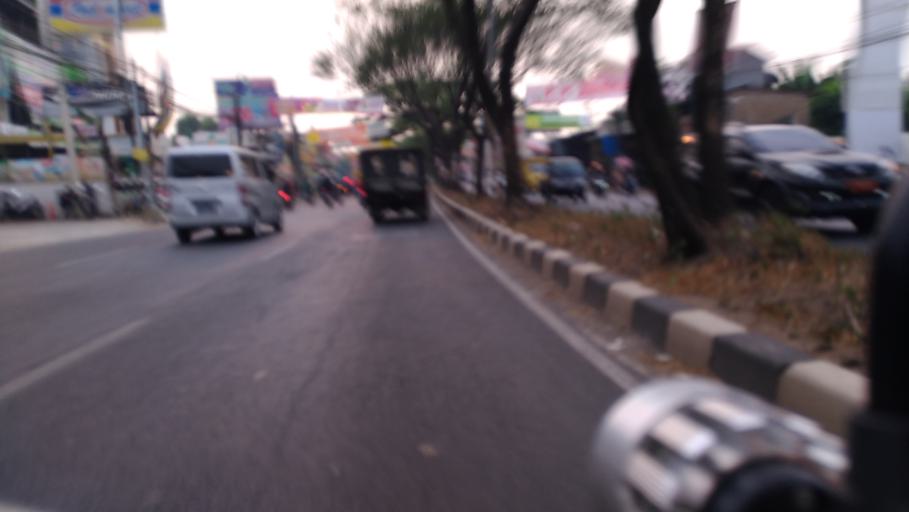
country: ID
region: West Java
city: Cileungsir
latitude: -6.3881
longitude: 106.9415
